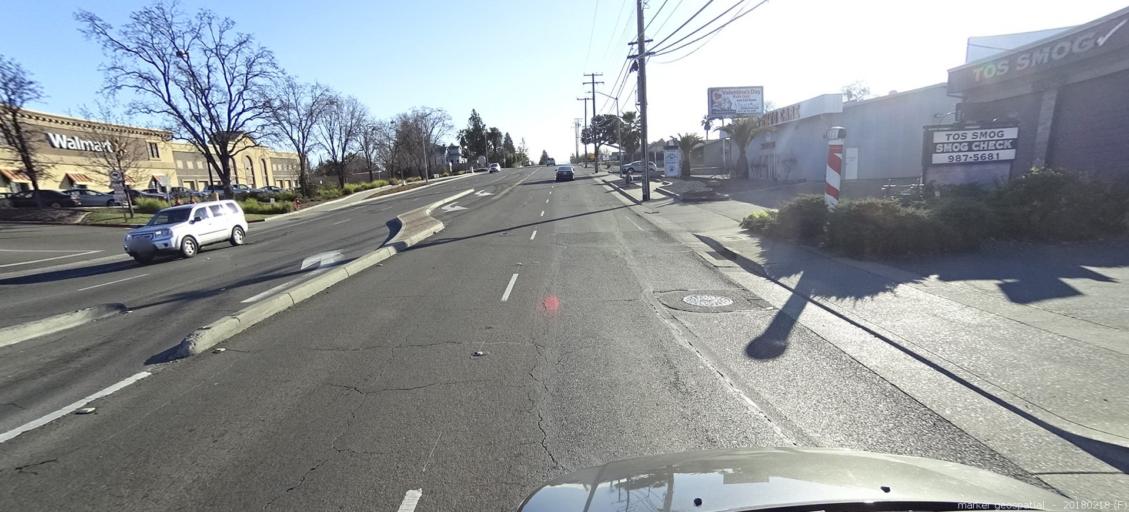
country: US
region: California
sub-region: Sacramento County
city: Orangevale
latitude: 38.6784
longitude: -121.2236
